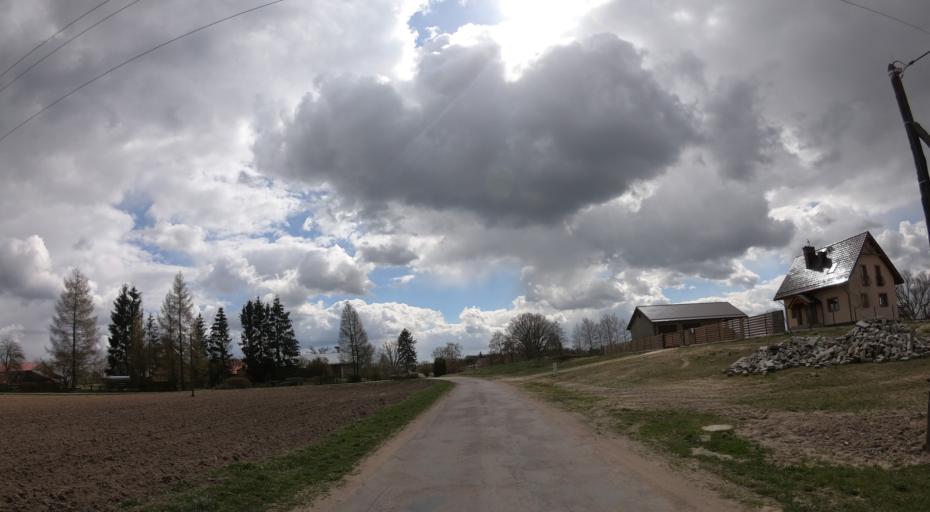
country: PL
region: West Pomeranian Voivodeship
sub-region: Powiat drawski
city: Drawsko Pomorskie
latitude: 53.5273
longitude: 15.8863
